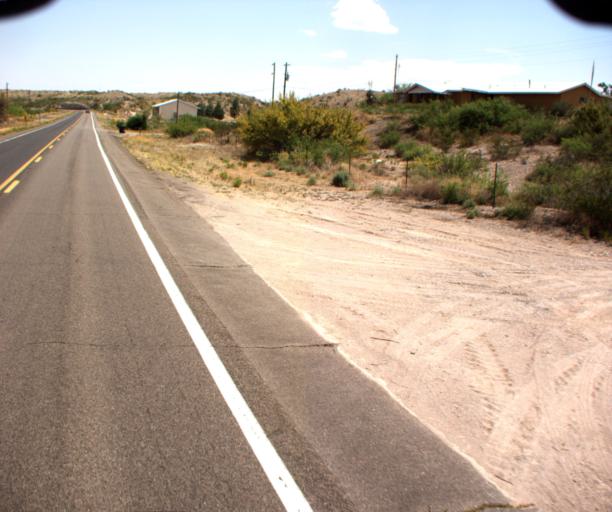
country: US
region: Arizona
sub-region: Greenlee County
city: Clifton
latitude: 32.7392
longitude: -109.1260
